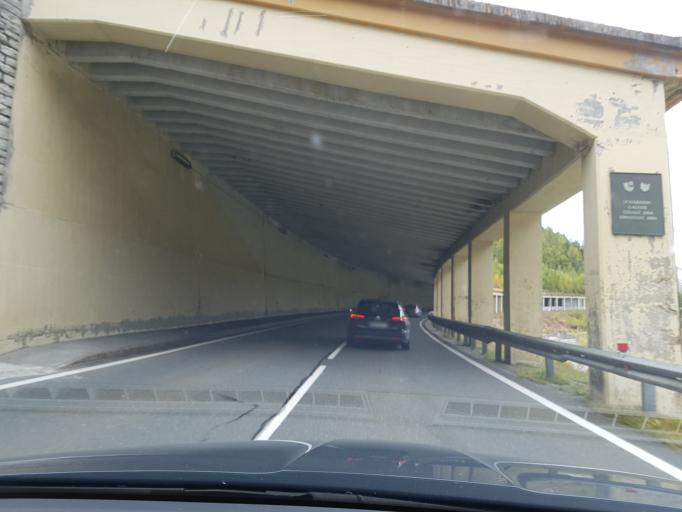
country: AT
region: Salzburg
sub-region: Politischer Bezirk Tamsweg
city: Tweng
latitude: 47.2384
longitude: 13.5724
